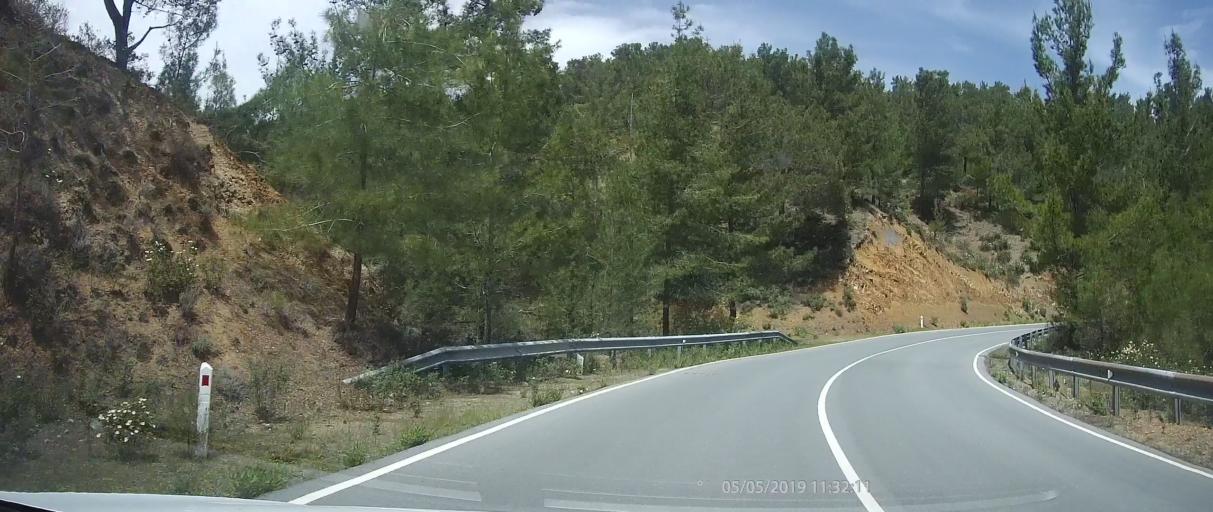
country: CY
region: Limassol
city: Pachna
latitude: 34.9534
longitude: 32.6450
